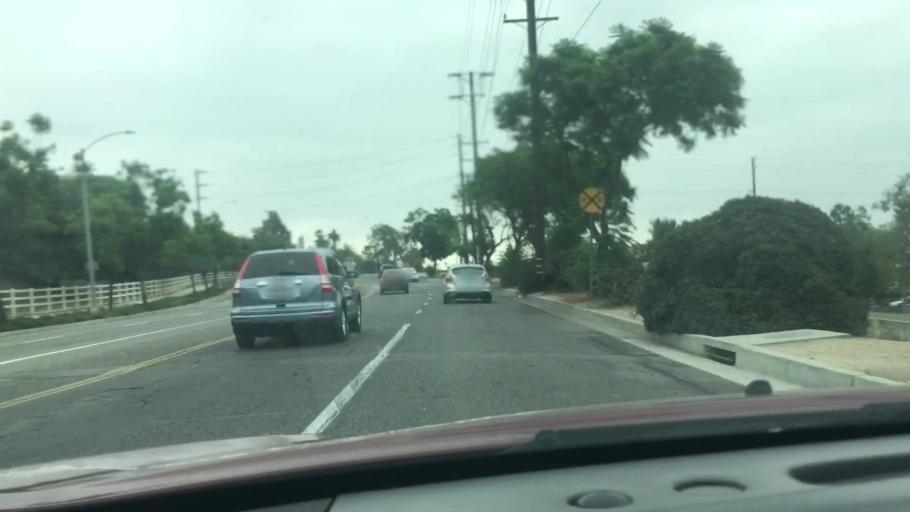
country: US
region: California
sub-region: Orange County
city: Fullerton
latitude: 33.8770
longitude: -117.9610
